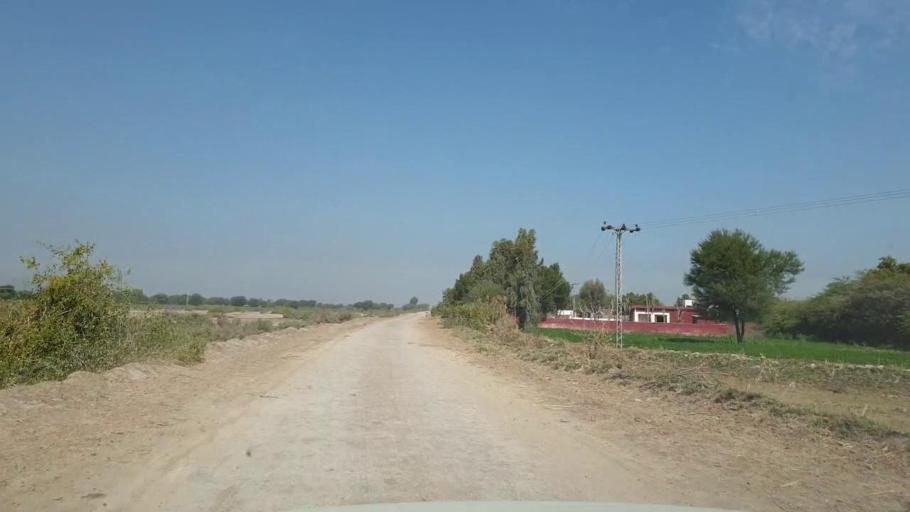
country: PK
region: Sindh
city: Pithoro
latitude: 25.5788
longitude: 69.2011
